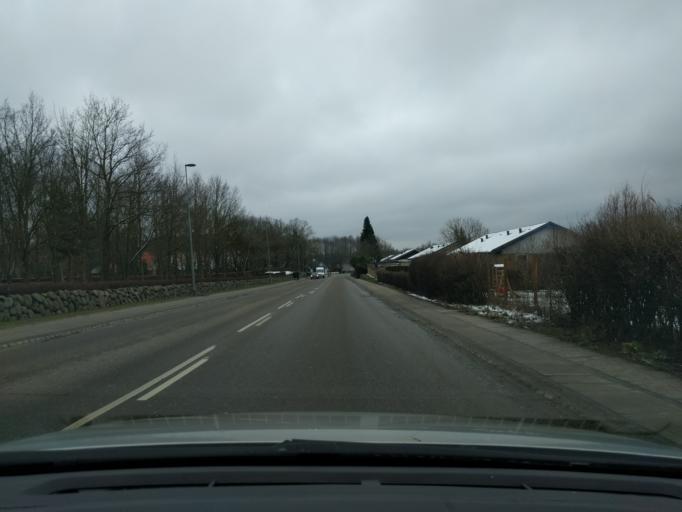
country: DK
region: South Denmark
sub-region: Odense Kommune
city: Bellinge
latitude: 55.3681
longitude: 10.3282
